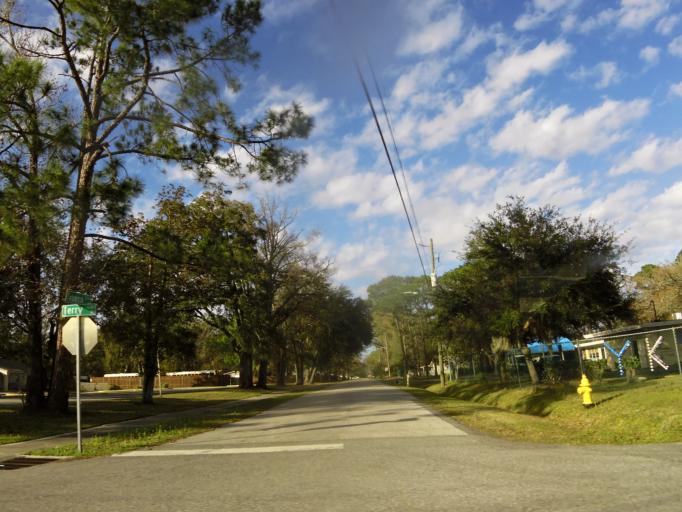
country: US
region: Florida
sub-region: Duval County
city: Jacksonville
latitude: 30.2774
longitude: -81.6007
